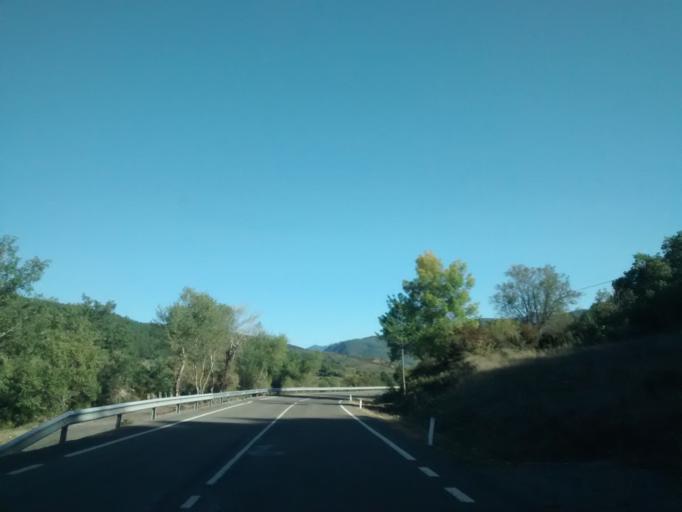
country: ES
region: Aragon
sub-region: Provincia de Huesca
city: Santa Cruz de la Seros
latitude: 42.6054
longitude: -0.7296
